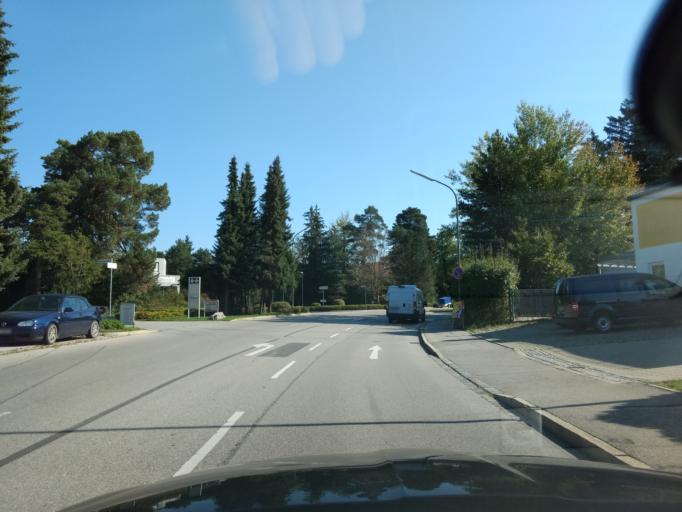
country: DE
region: Bavaria
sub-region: Upper Bavaria
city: Geretsried
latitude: 47.8844
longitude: 11.4610
